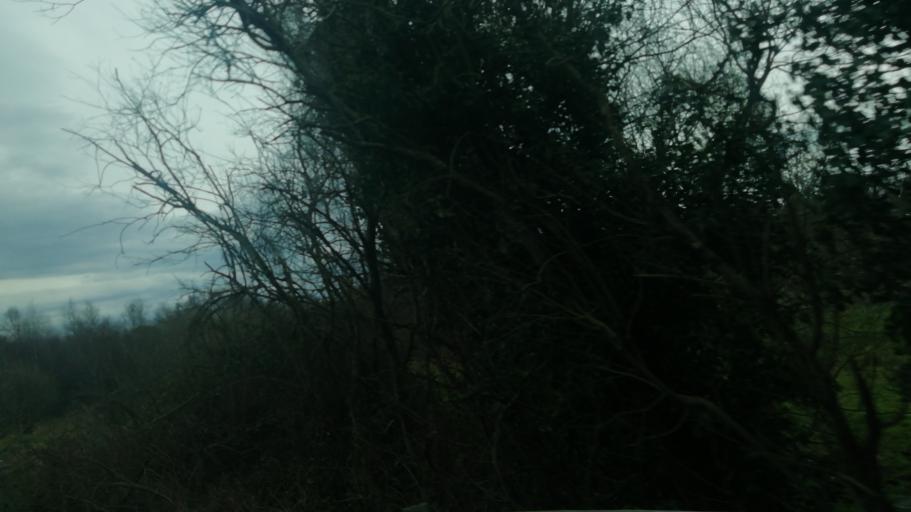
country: IE
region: Leinster
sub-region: Kildare
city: Prosperous
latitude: 53.2852
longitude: -6.8276
